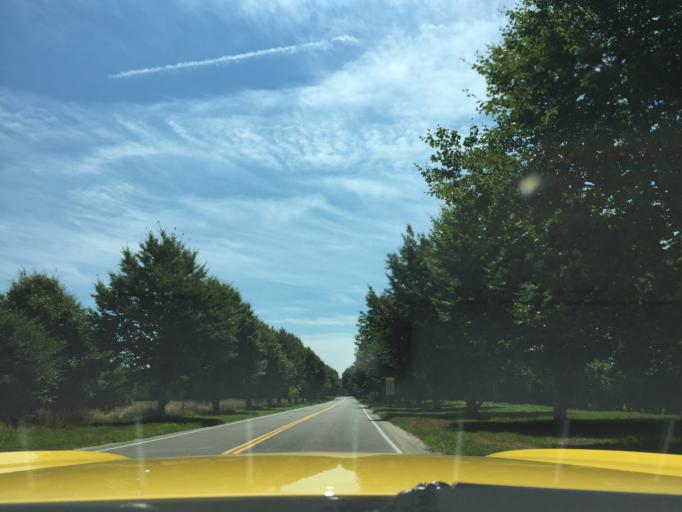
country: US
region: New York
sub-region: Suffolk County
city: Bridgehampton
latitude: 40.9312
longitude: -72.2833
